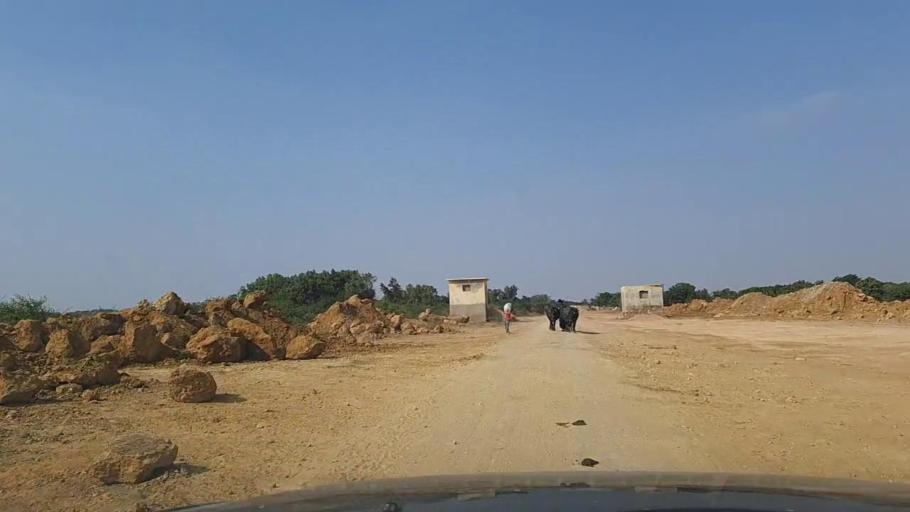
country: PK
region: Sindh
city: Gharo
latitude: 24.7619
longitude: 67.5783
